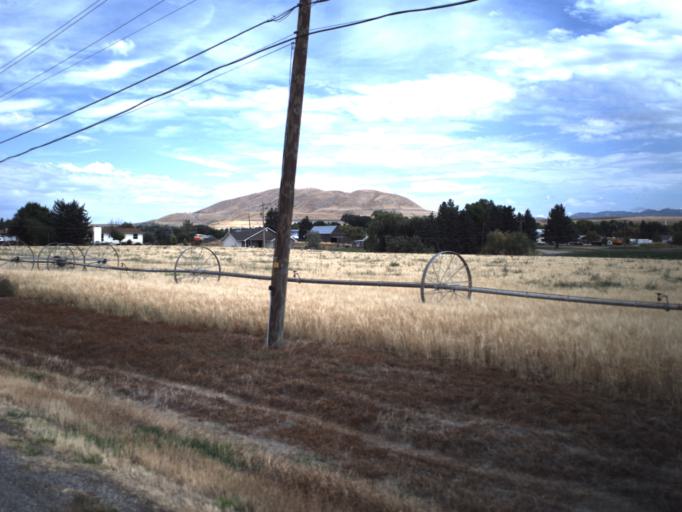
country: US
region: Utah
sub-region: Cache County
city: Benson
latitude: 41.8569
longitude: -112.0000
